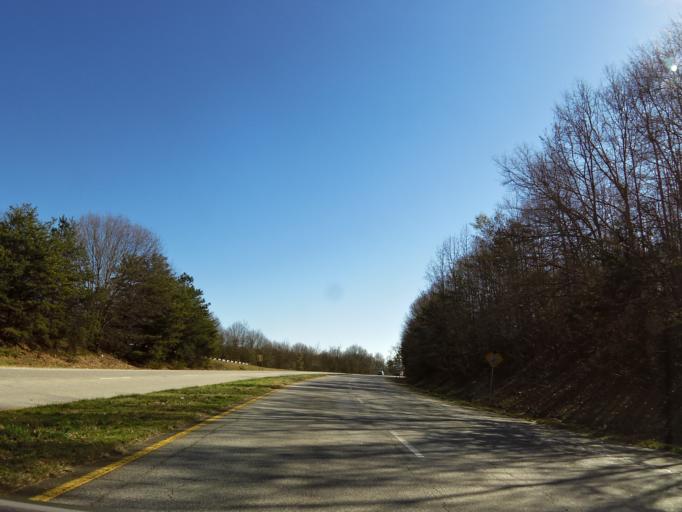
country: US
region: South Carolina
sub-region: Greenville County
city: Sans Souci
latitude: 34.9145
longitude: -82.4282
